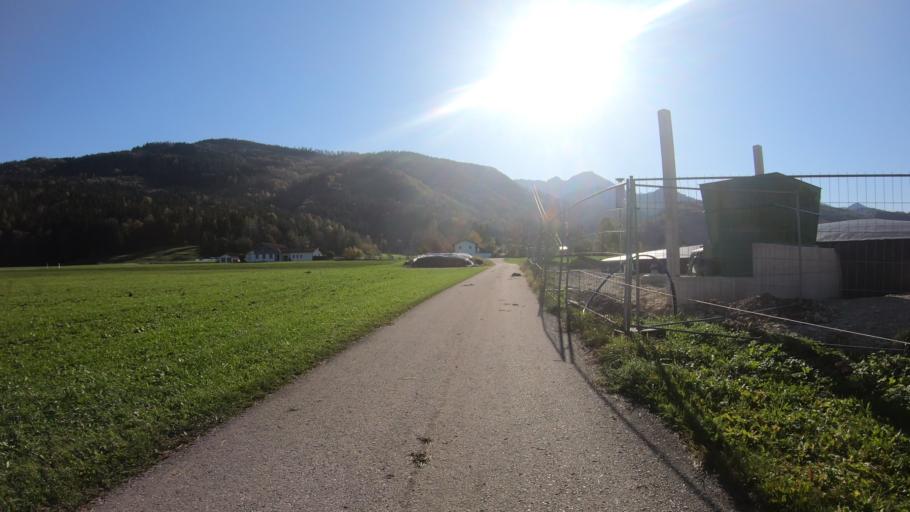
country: DE
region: Bavaria
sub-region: Upper Bavaria
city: Bergen
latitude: 47.8030
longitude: 12.5954
